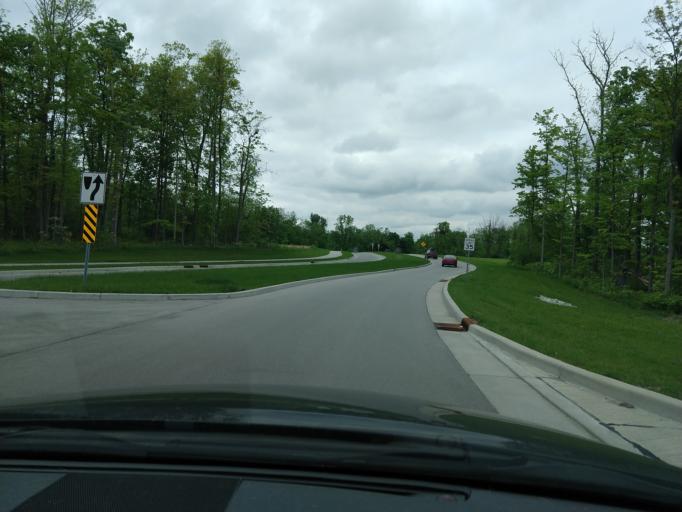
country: US
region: Indiana
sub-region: Hamilton County
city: Carmel
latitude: 40.0093
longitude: -86.1306
